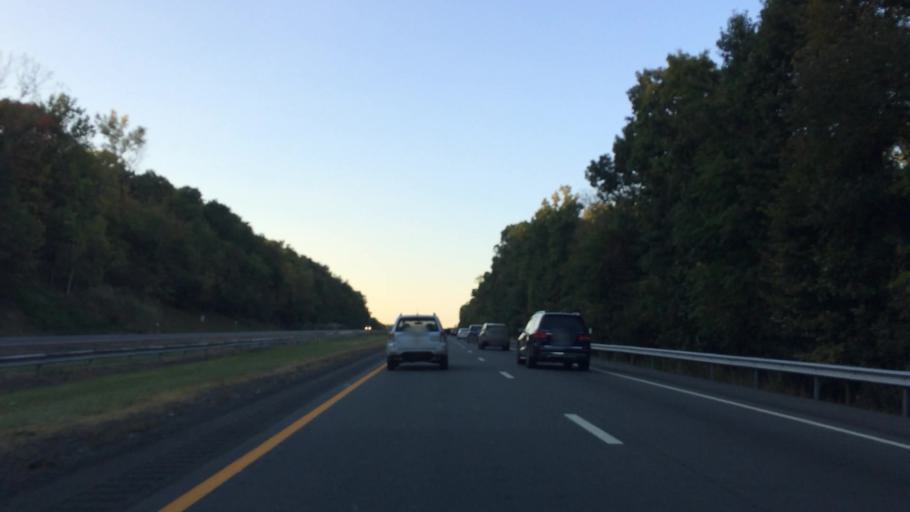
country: US
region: New York
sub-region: Orange County
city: Vails Gate
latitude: 41.4593
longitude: -74.0662
